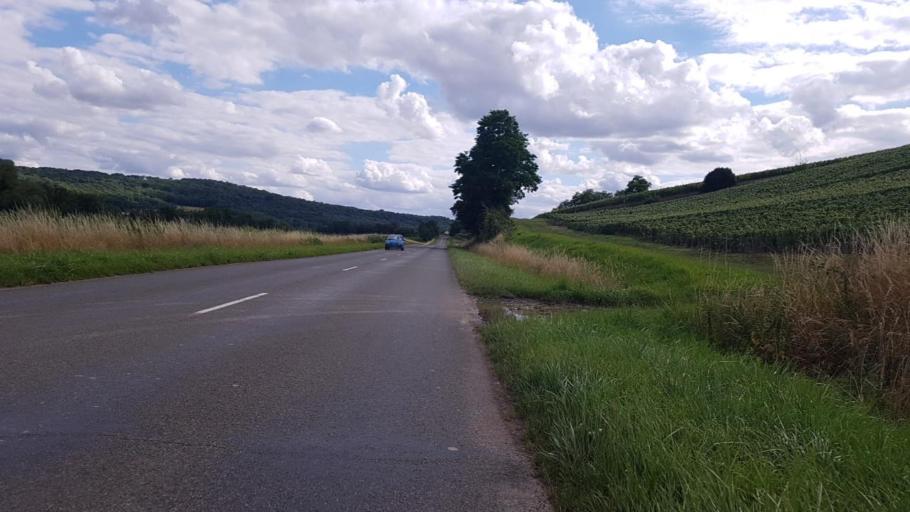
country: FR
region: Picardie
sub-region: Departement de l'Aisne
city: Crezancy
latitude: 49.0592
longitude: 3.4755
